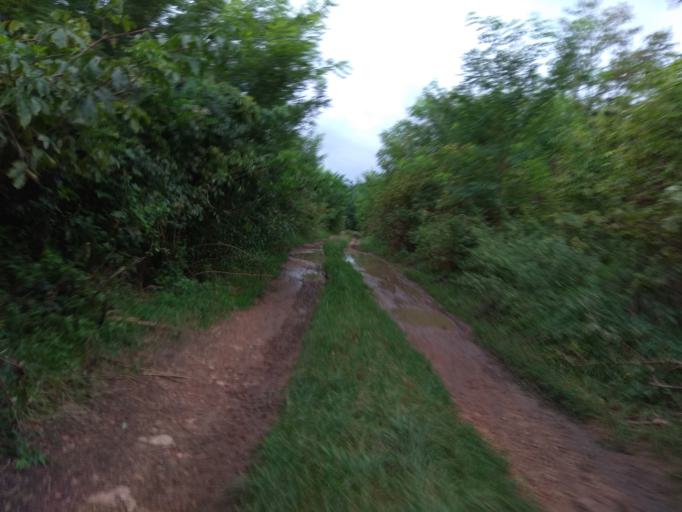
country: HU
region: Borsod-Abauj-Zemplen
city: Monok
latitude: 48.1765
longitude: 21.1219
